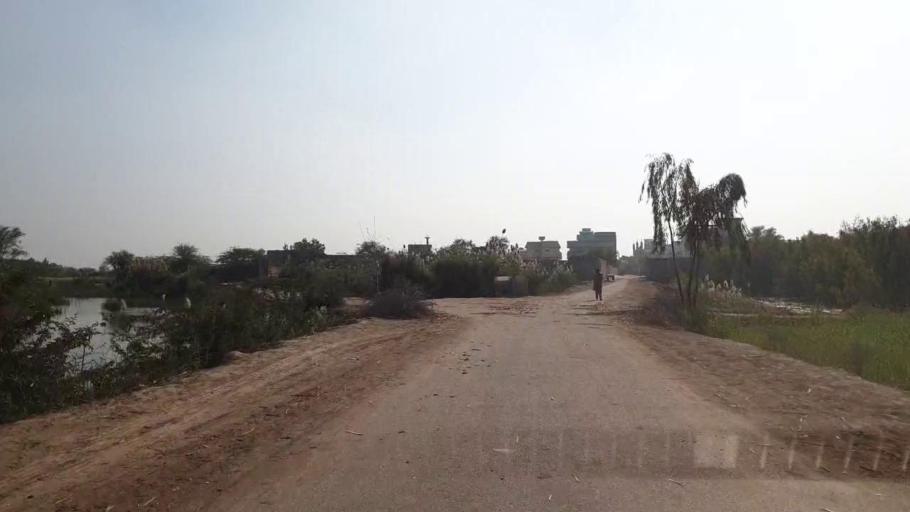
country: PK
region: Sindh
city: Tando Adam
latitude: 25.6611
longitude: 68.5764
